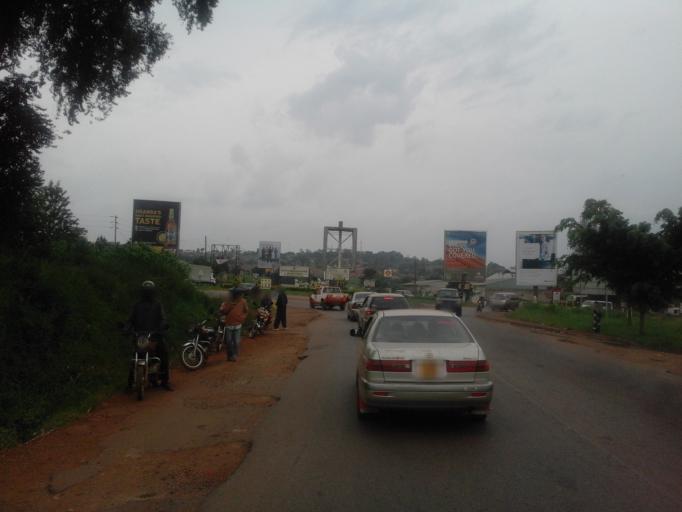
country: UG
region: Eastern Region
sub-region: Jinja District
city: Jinja
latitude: 0.4449
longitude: 33.1971
